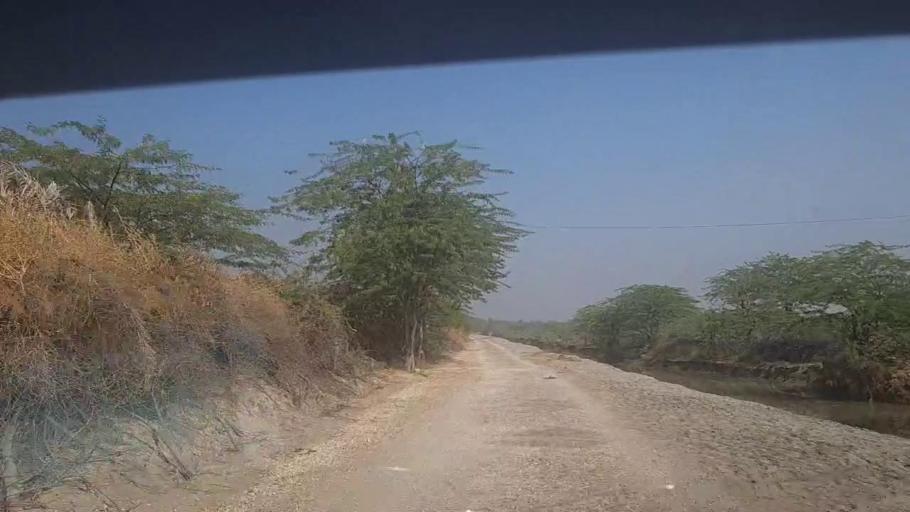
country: PK
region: Sindh
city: Khairpur
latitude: 27.4536
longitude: 68.7228
